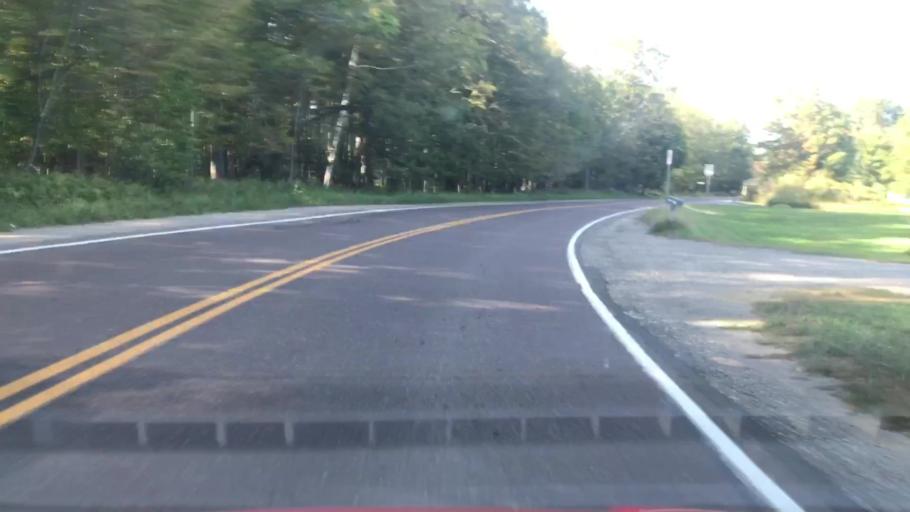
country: US
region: Michigan
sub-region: Chippewa County
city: Sault Ste. Marie
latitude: 46.2810
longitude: -84.0322
